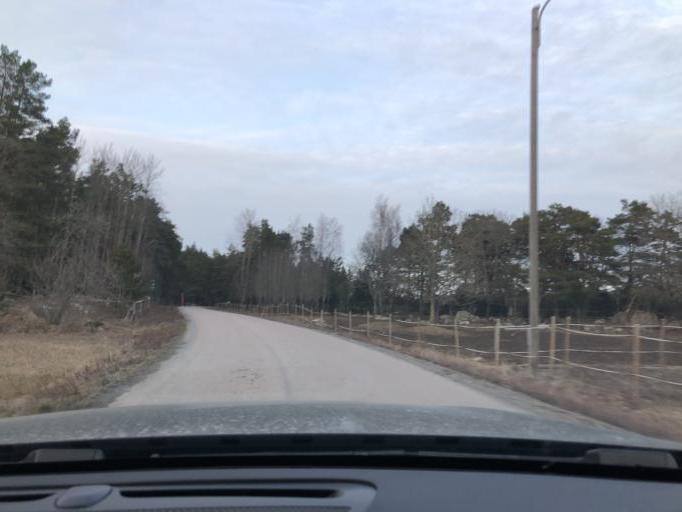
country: SE
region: Uppsala
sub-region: Uppsala Kommun
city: Gamla Uppsala
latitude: 59.9209
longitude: 17.6494
